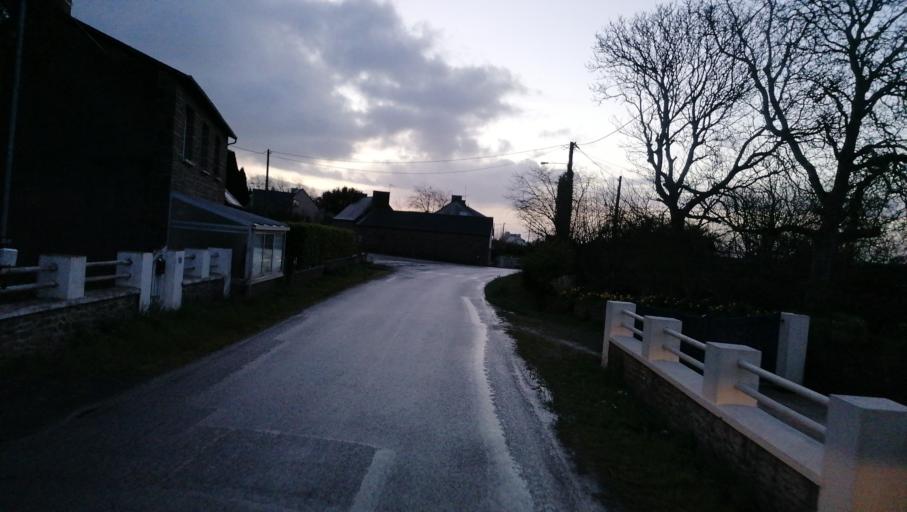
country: FR
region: Brittany
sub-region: Departement des Cotes-d'Armor
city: Plouha
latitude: 48.6710
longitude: -2.9633
